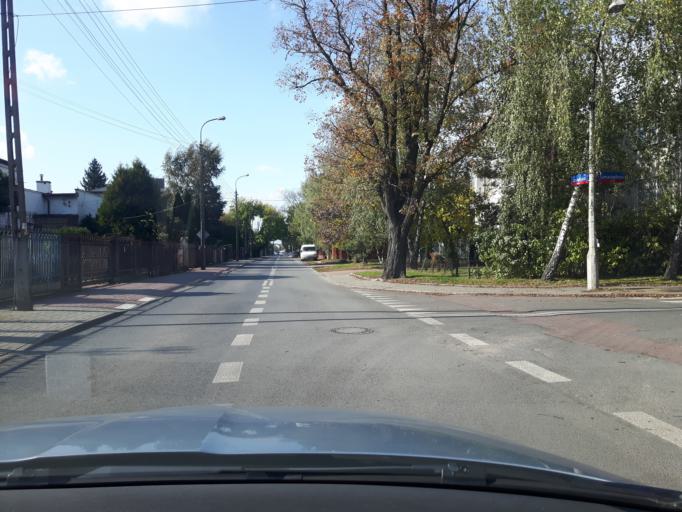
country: PL
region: Masovian Voivodeship
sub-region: Powiat wolominski
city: Zabki
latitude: 52.2792
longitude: 21.0773
